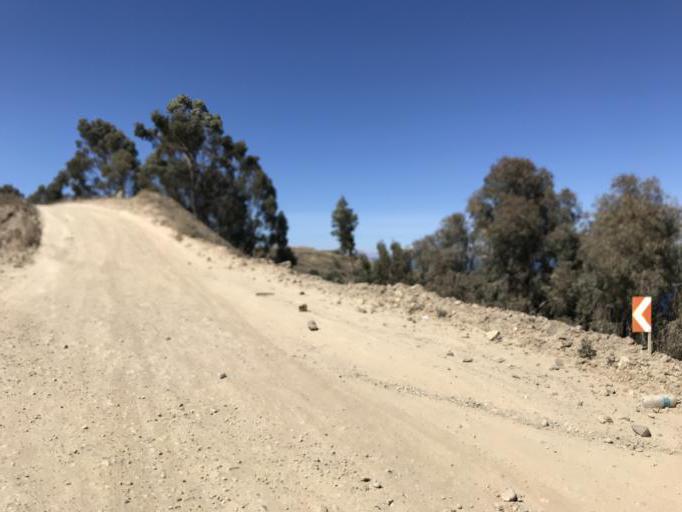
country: BO
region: La Paz
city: San Pablo
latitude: -16.1983
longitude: -68.8294
